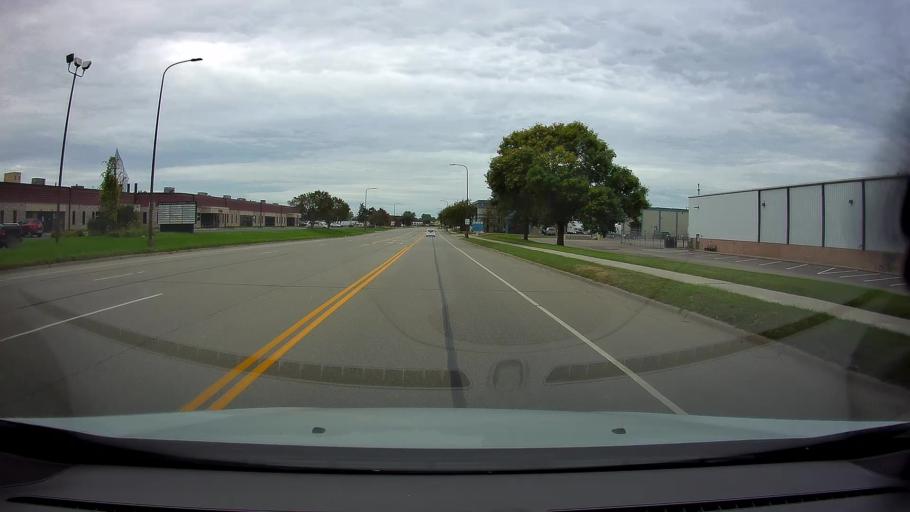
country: US
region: Minnesota
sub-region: Ramsey County
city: Falcon Heights
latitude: 44.9655
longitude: -93.1858
